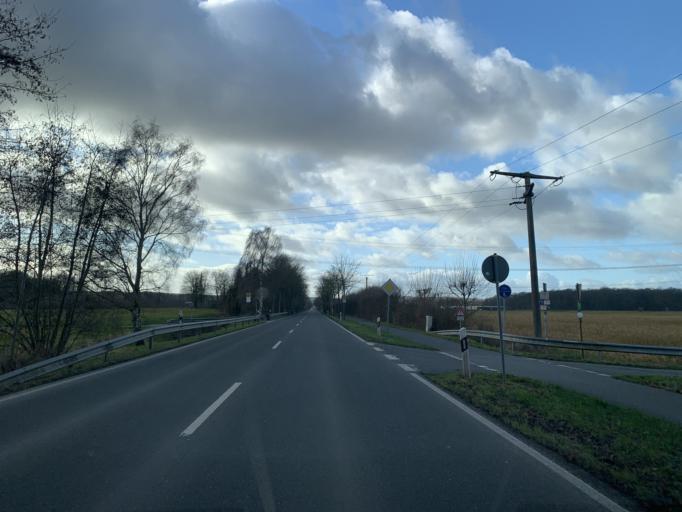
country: DE
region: North Rhine-Westphalia
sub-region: Regierungsbezirk Munster
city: Havixbeck
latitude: 51.9851
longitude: 7.4464
